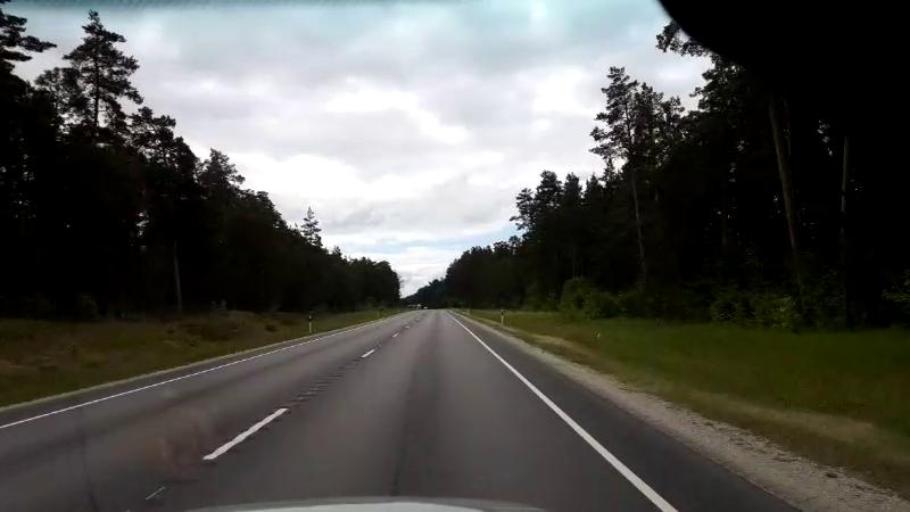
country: EE
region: Paernumaa
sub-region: Paernu linn
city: Parnu
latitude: 58.1752
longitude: 24.4939
